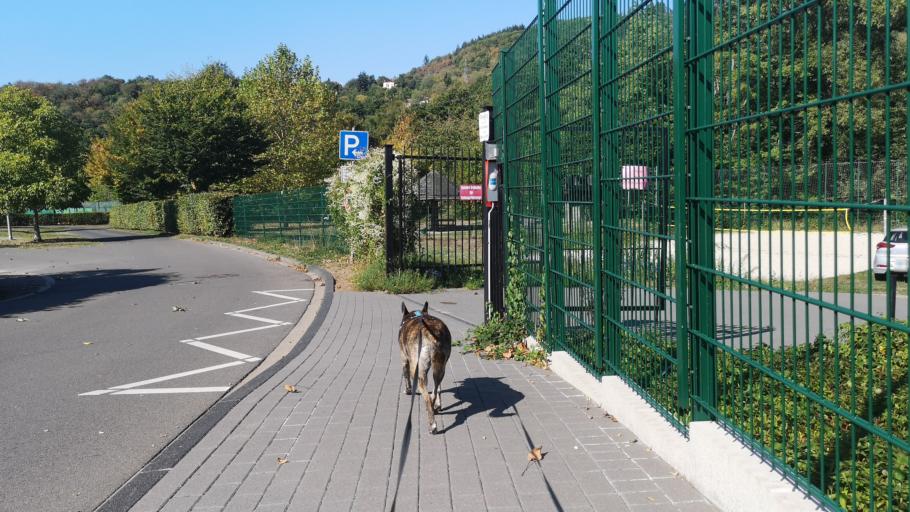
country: DE
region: North Rhine-Westphalia
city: Heimbach
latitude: 50.6380
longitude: 6.4699
